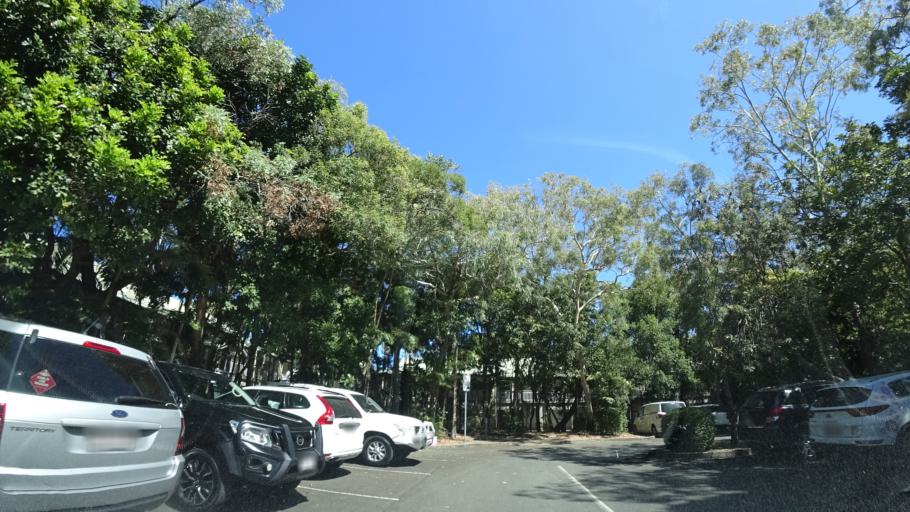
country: AU
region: Queensland
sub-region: Sunshine Coast
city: Mooloolaba
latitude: -26.6339
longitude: 153.0961
